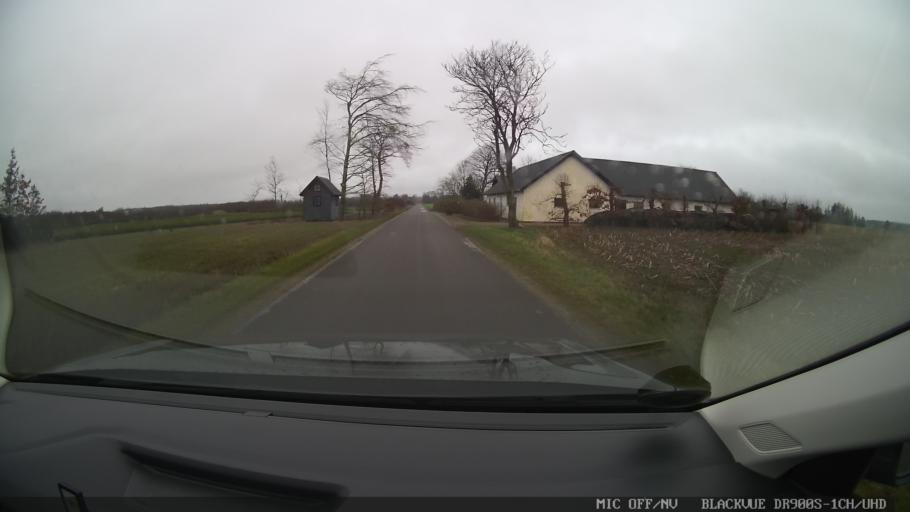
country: DK
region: Central Jutland
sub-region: Viborg Kommune
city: Karup
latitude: 56.3112
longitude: 9.2443
